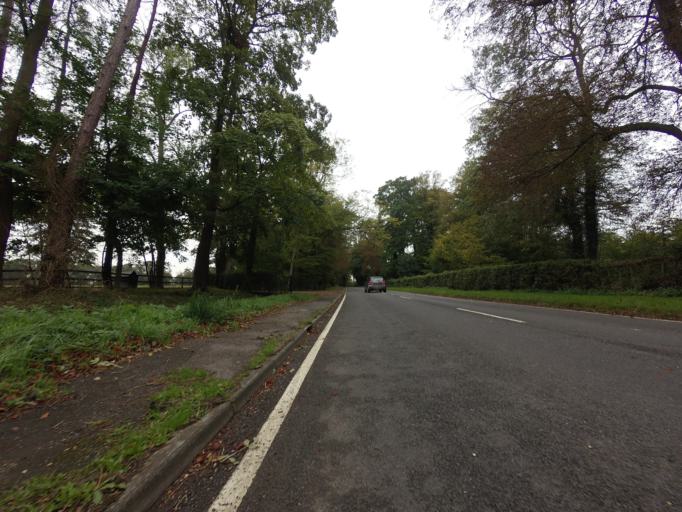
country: GB
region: England
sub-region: Hertfordshire
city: Reed
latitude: 52.0084
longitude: 0.0226
